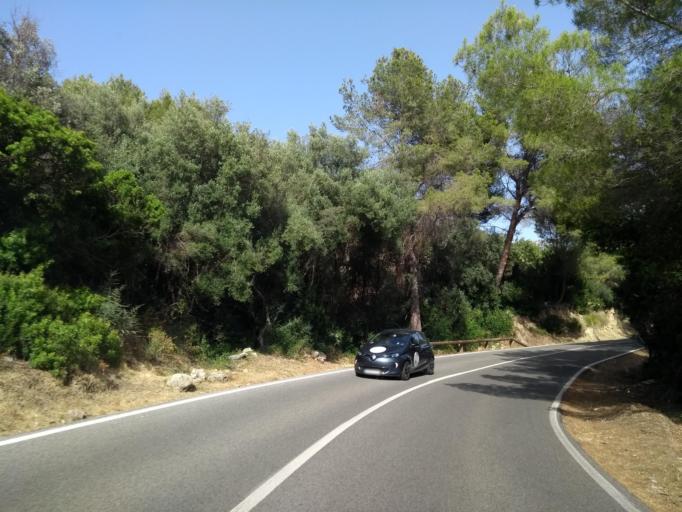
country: ES
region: Balearic Islands
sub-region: Illes Balears
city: Soller
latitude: 39.7831
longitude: 2.7134
